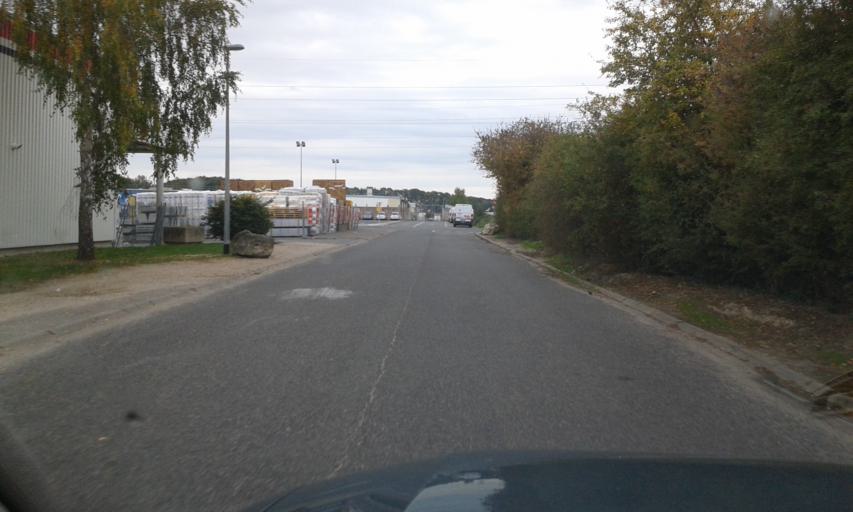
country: FR
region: Centre
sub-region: Departement du Loiret
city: Saran
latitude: 47.9626
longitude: 1.8841
